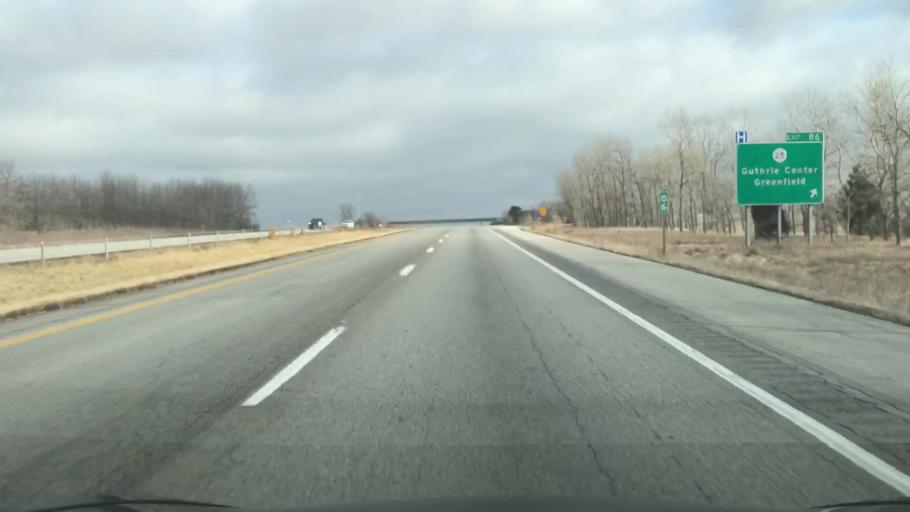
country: US
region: Iowa
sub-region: Guthrie County
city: Stuart
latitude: 41.4957
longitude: -94.4579
